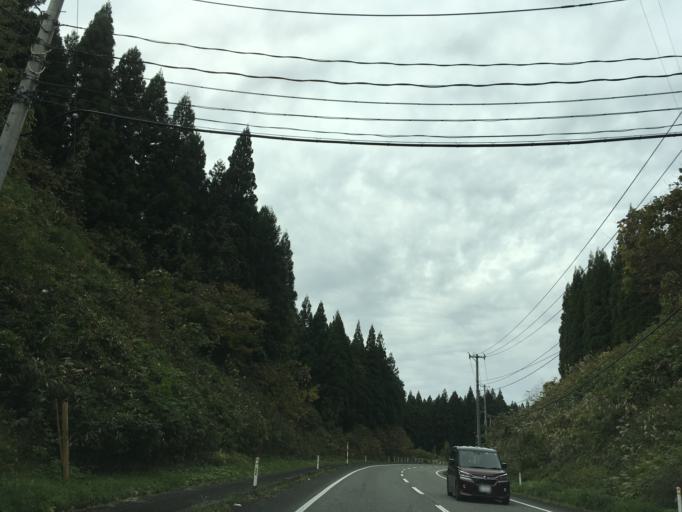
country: JP
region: Miyagi
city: Furukawa
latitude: 38.8017
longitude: 140.8256
